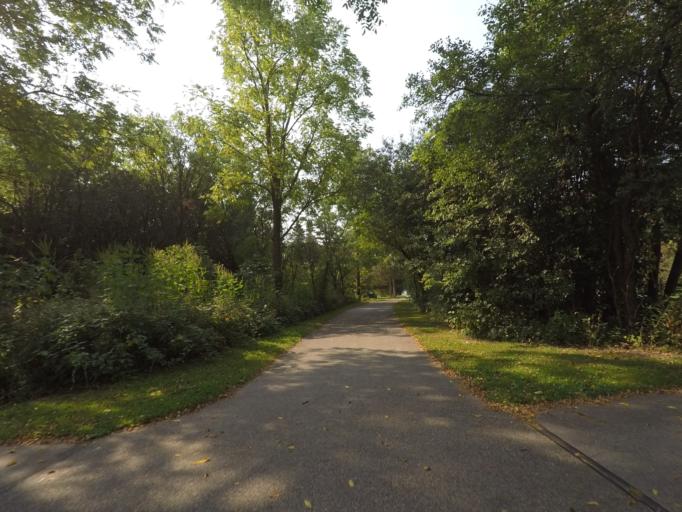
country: US
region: Wisconsin
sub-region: Waukesha County
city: Delafield
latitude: 43.0345
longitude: -88.4142
